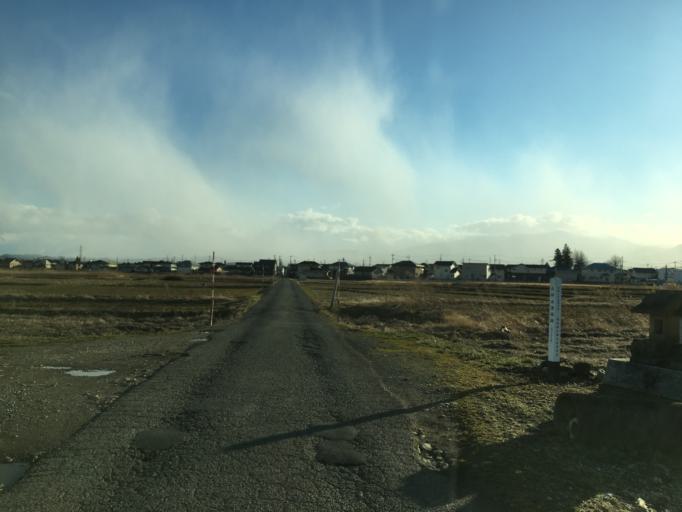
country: JP
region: Fukushima
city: Fukushima-shi
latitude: 37.7738
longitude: 140.4309
